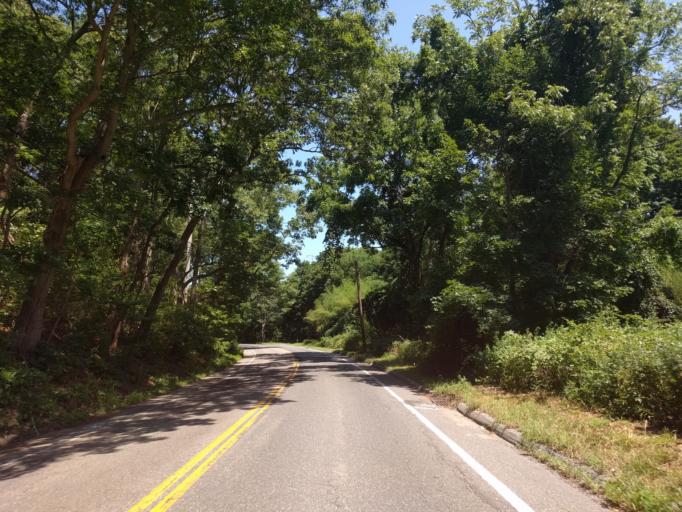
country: US
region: New York
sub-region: Suffolk County
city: Fort Salonga
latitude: 40.9037
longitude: -73.2966
